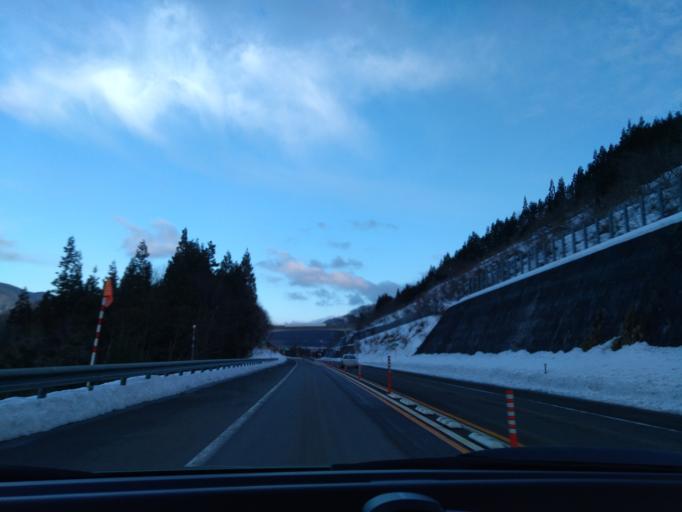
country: JP
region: Akita
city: Yokotemachi
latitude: 39.2980
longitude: 140.8239
